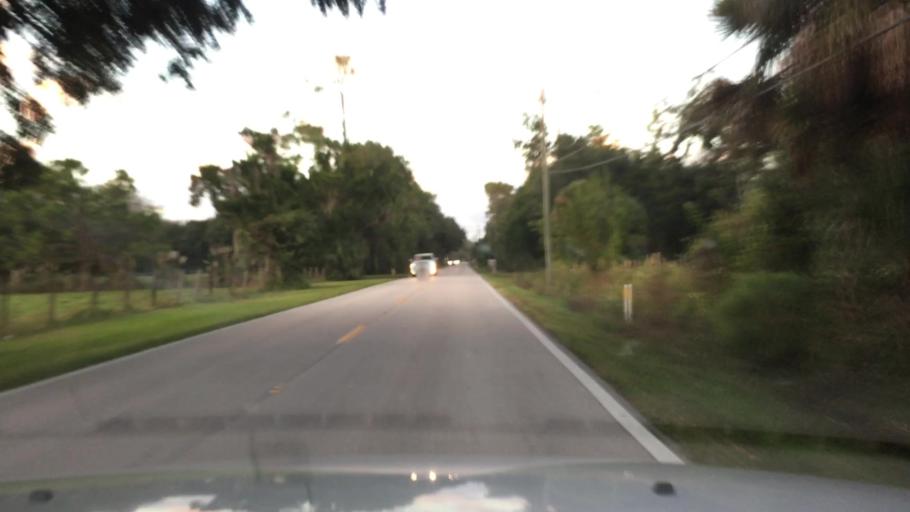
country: US
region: Florida
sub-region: Volusia County
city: Ormond Beach
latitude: 29.2828
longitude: -81.1130
